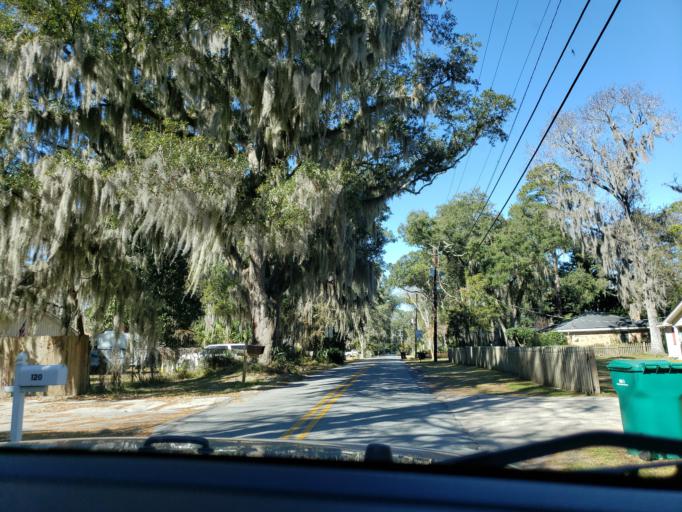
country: US
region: Georgia
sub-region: Chatham County
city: Whitemarsh Island
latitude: 32.0424
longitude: -80.9958
